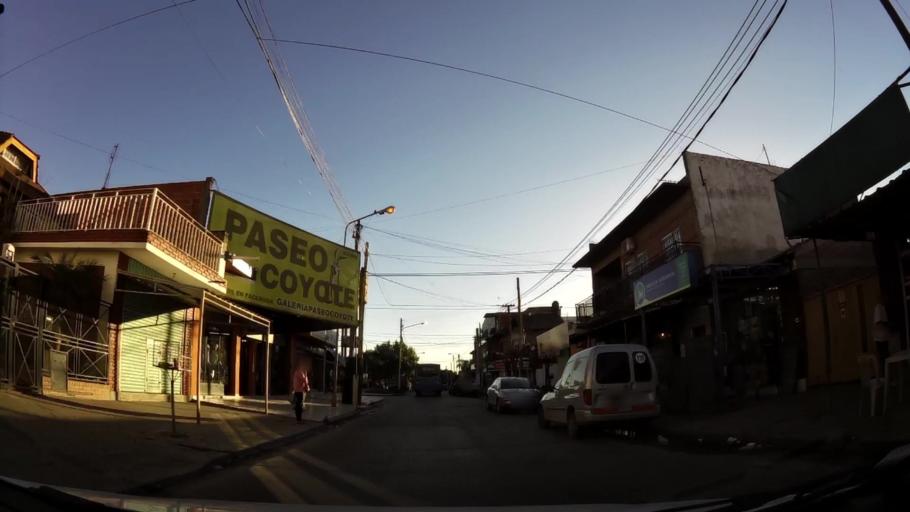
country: AR
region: Buenos Aires
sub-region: Partido de Moron
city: Moron
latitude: -34.7141
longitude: -58.6133
